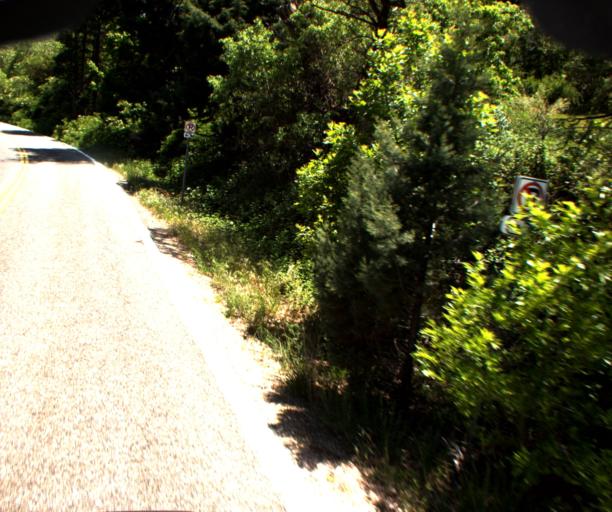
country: US
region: Arizona
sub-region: Coconino County
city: Sedona
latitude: 34.9411
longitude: -111.7512
